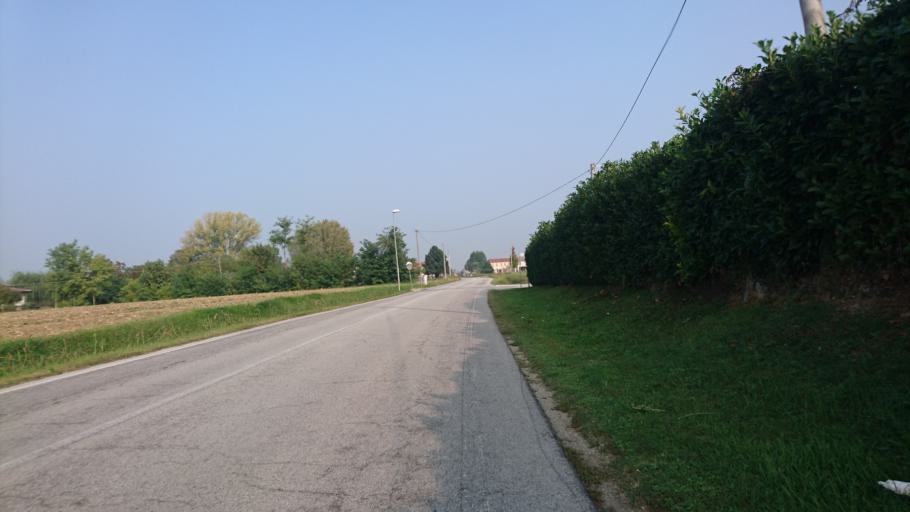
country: IT
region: Veneto
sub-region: Provincia di Padova
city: Curtarolo
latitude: 45.5281
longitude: 11.8420
